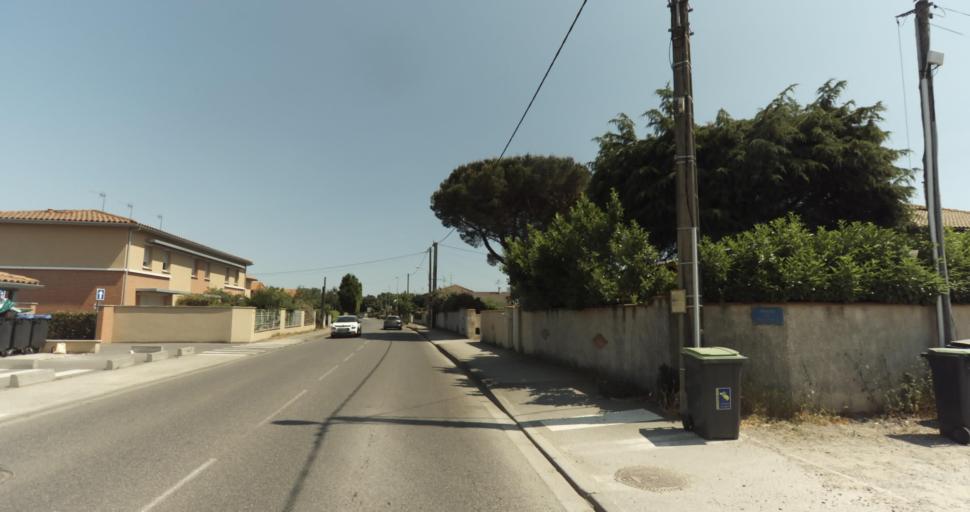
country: FR
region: Midi-Pyrenees
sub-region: Departement de la Haute-Garonne
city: La Salvetat-Saint-Gilles
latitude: 43.5740
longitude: 1.2710
